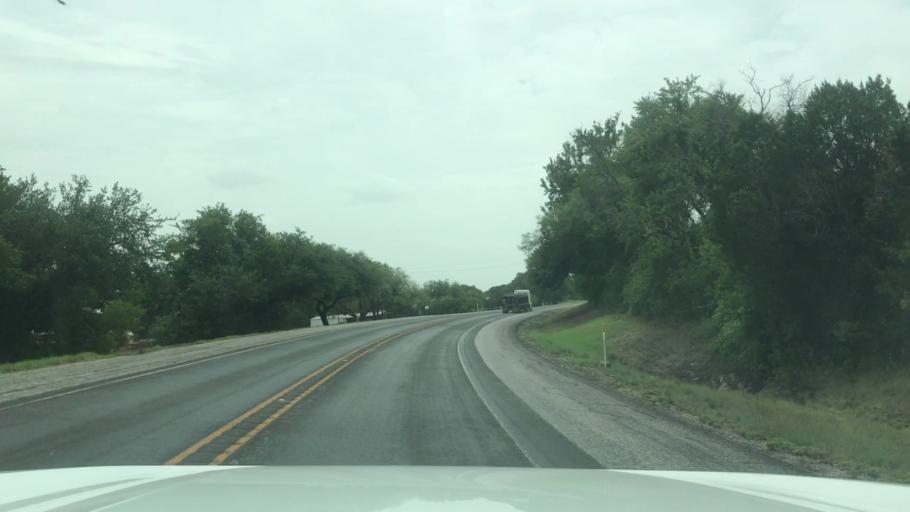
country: US
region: Texas
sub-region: Bosque County
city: Meridian
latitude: 31.8963
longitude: -97.6479
